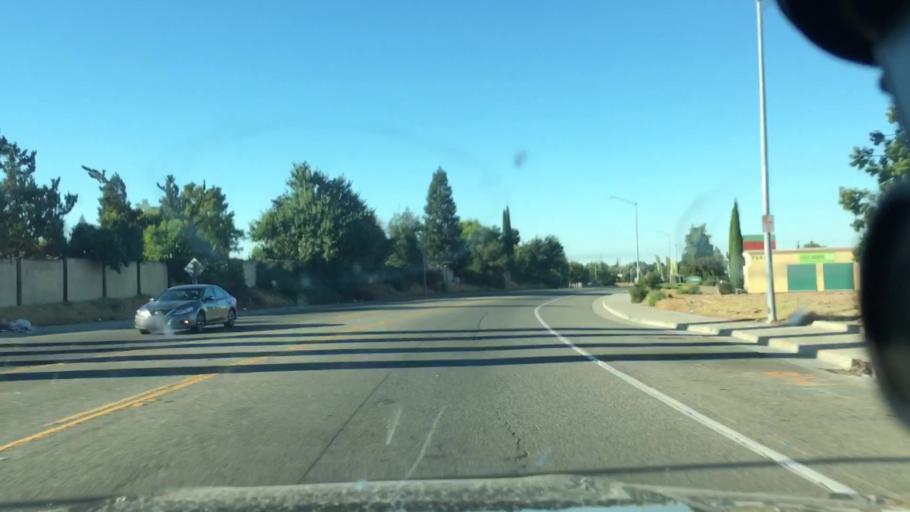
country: US
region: California
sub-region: Sacramento County
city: Antelope
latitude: 38.7004
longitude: -121.3325
